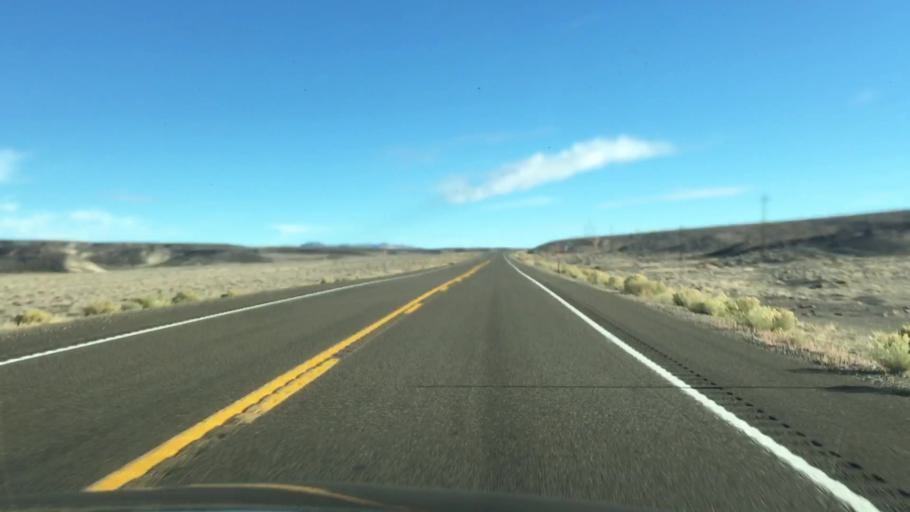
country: US
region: Nevada
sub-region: Mineral County
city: Hawthorne
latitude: 38.2337
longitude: -118.0236
